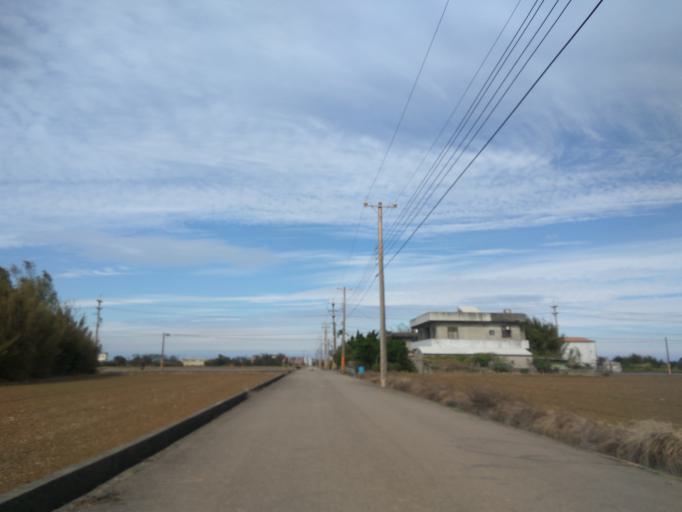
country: TW
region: Taiwan
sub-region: Hsinchu
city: Zhubei
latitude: 24.9867
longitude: 121.0881
